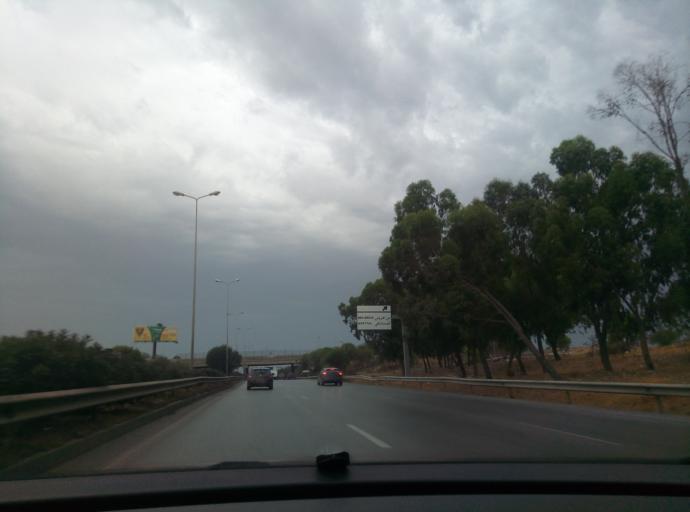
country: TN
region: Bin 'Arus
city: Ben Arous
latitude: 36.7479
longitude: 10.2084
